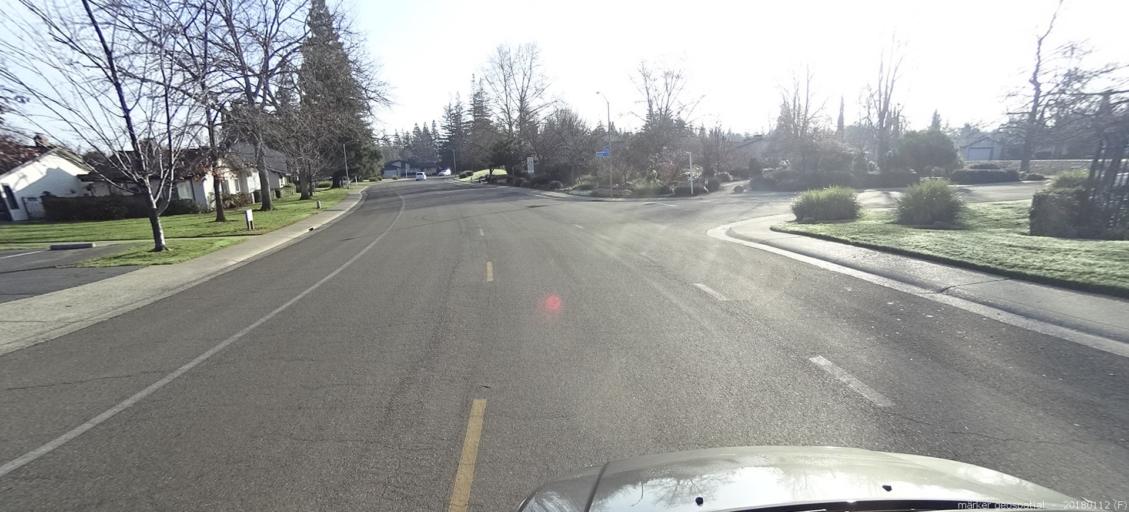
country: US
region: California
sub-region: Sacramento County
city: Fair Oaks
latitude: 38.6157
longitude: -121.2777
